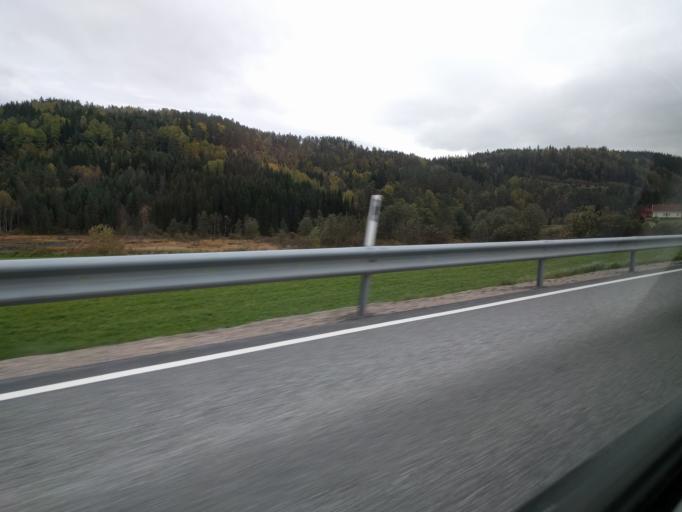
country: NO
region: Aust-Agder
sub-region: Iveland
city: Birketveit
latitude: 58.4052
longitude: 7.7668
